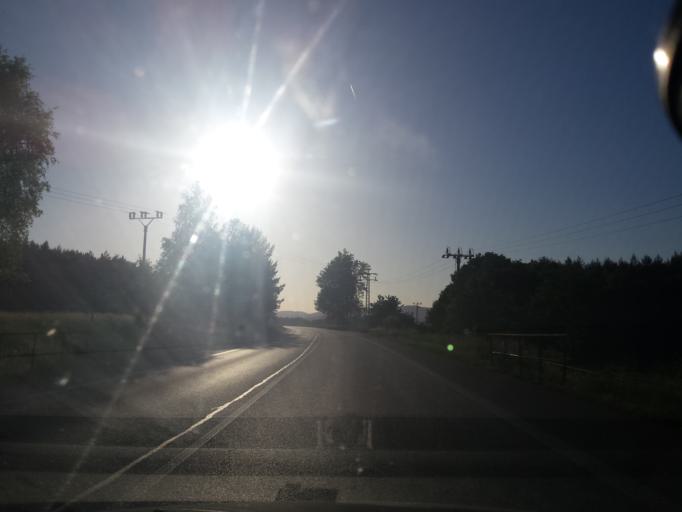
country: CZ
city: Duba
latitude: 50.6129
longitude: 14.5738
